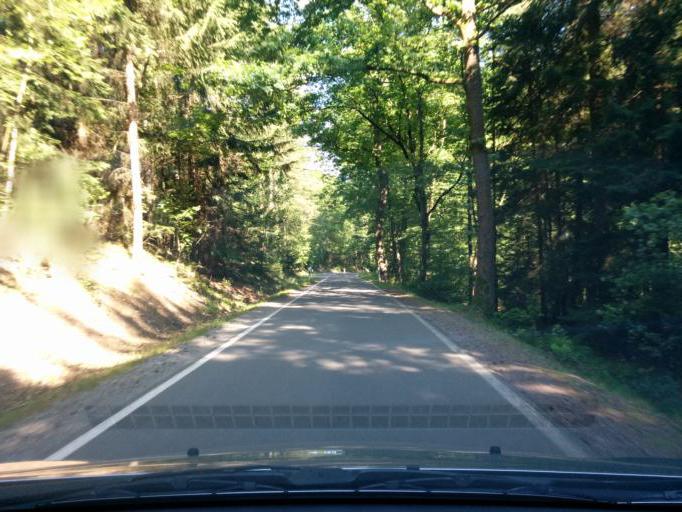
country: DE
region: Saxony
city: Floha
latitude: 50.8427
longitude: 13.0605
